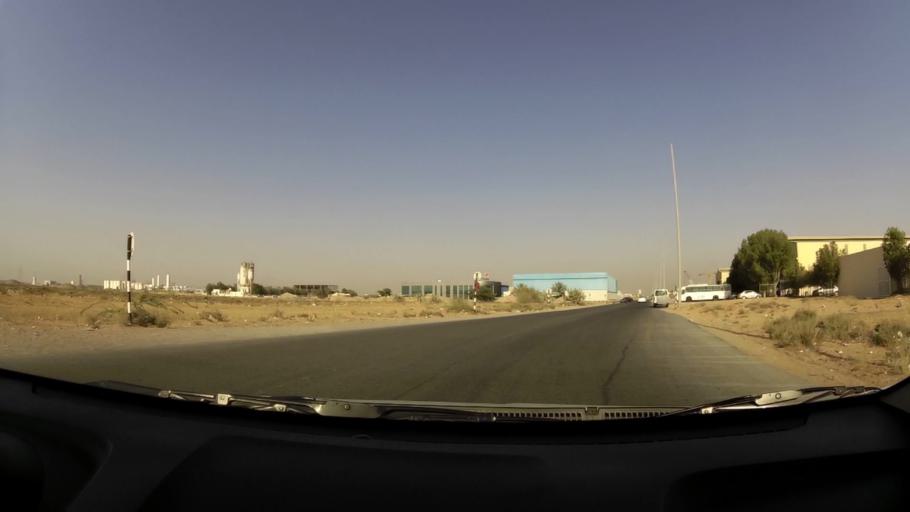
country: AE
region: Umm al Qaywayn
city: Umm al Qaywayn
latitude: 25.4396
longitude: 55.5669
